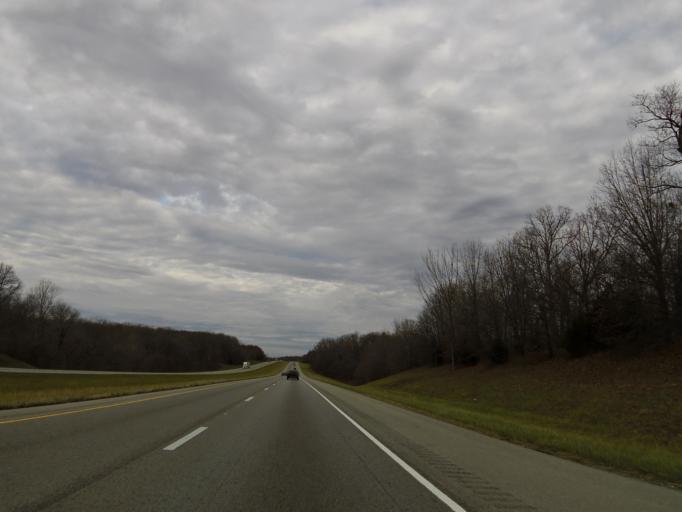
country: US
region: Illinois
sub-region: Clinton County
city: Wamac
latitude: 38.3686
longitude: -89.0914
